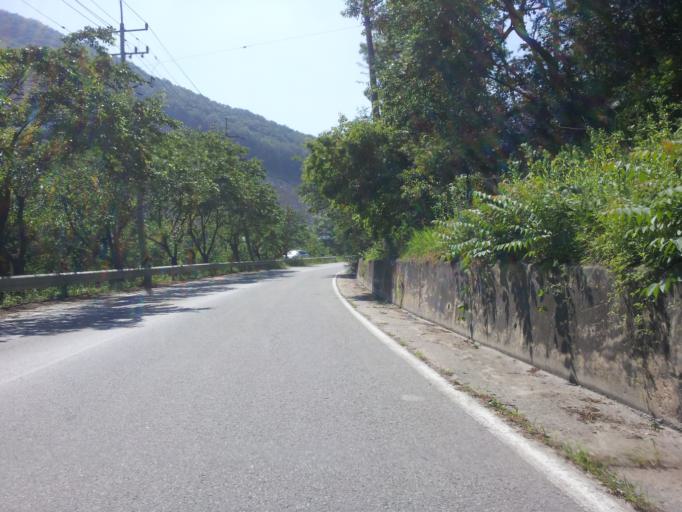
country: KR
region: Chungcheongbuk-do
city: Okcheon
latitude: 36.4523
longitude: 127.6786
